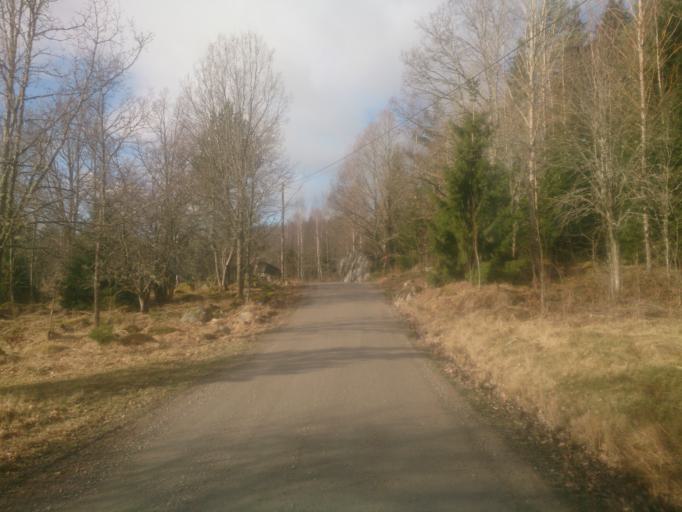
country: SE
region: OEstergoetland
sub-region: Atvidabergs Kommun
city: Atvidaberg
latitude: 58.2255
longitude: 16.1754
